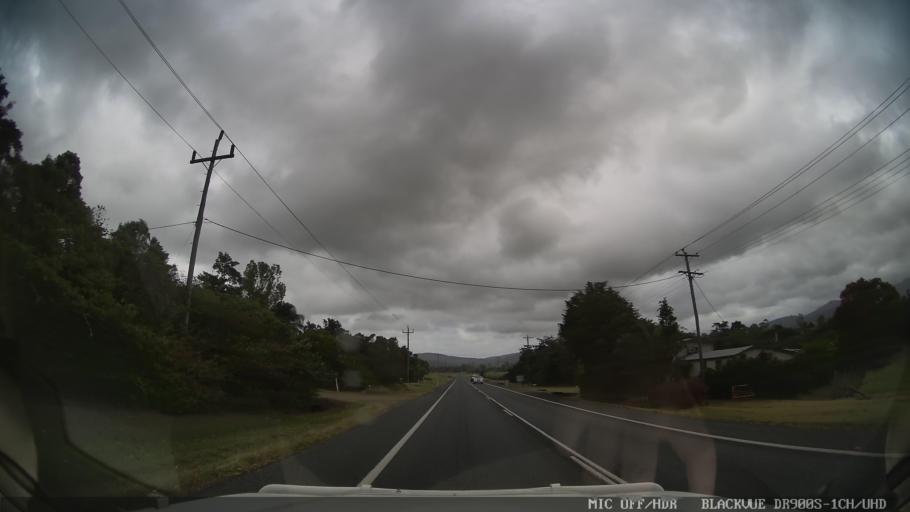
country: AU
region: Queensland
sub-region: Whitsunday
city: Proserpine
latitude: -20.3449
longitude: 148.6399
